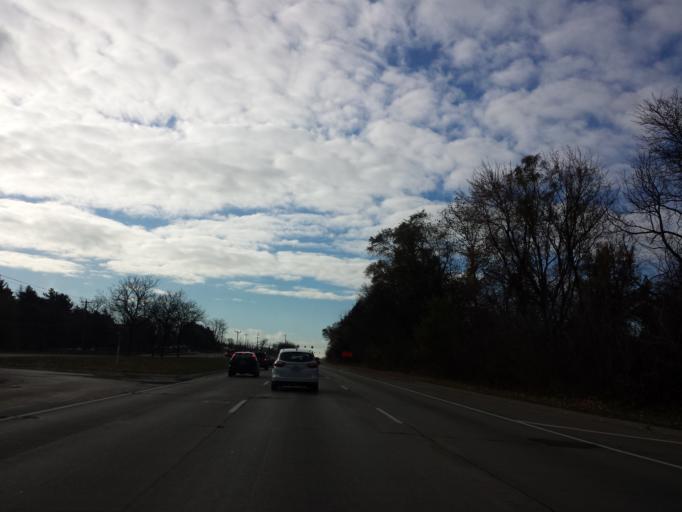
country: US
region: Michigan
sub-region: Oakland County
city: Bloomfield Hills
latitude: 42.5862
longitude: -83.2814
